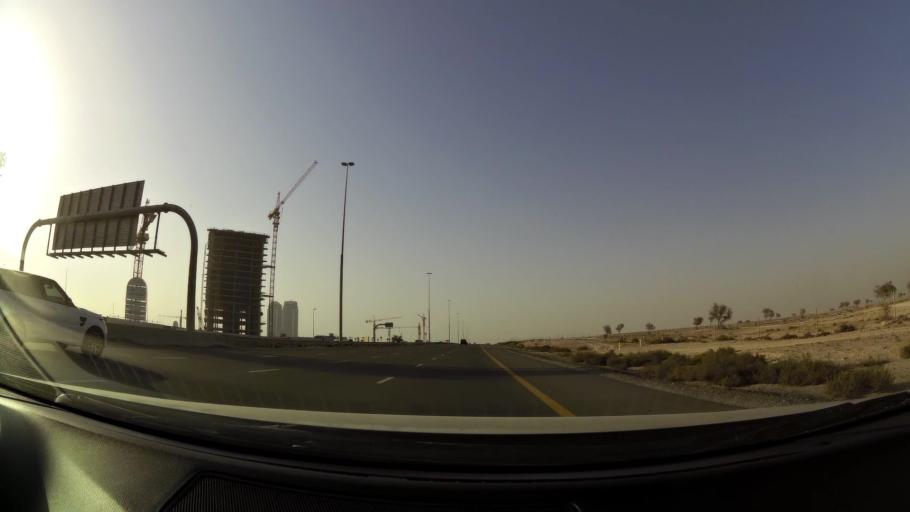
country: AE
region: Dubai
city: Dubai
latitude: 25.0714
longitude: 55.2501
